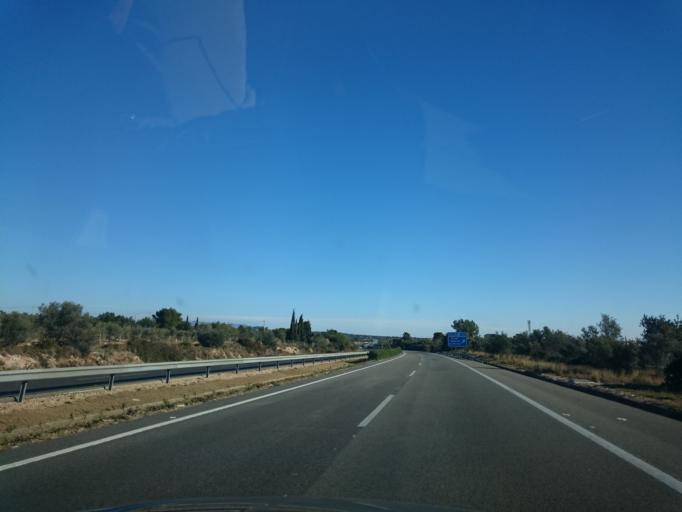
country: ES
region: Catalonia
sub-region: Provincia de Tarragona
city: L'Ampolla
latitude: 40.8055
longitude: 0.6922
